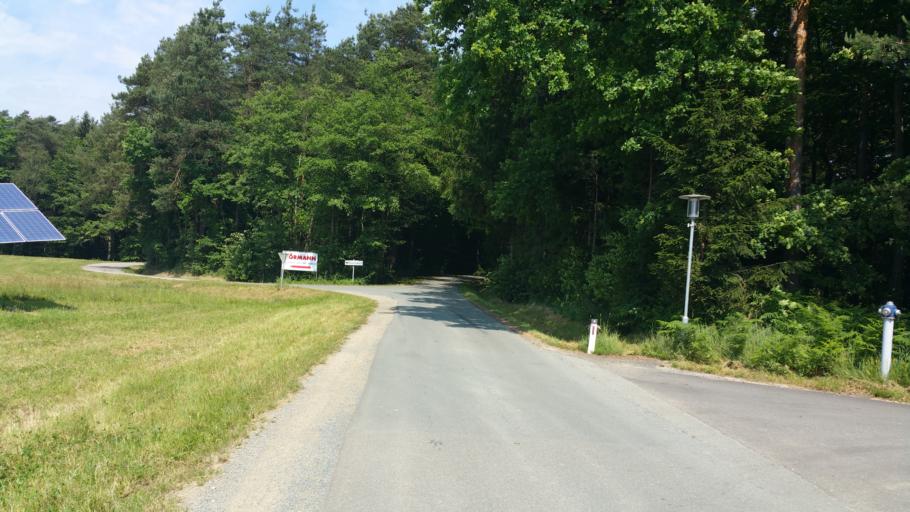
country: AT
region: Styria
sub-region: Politischer Bezirk Leibnitz
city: Pistorf
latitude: 46.7672
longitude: 15.3672
